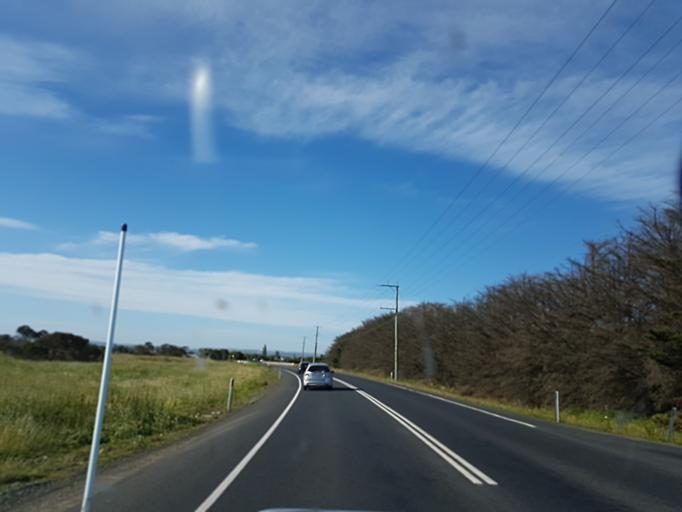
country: AU
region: Victoria
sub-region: Cardinia
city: Pakenham South
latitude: -38.1397
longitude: 145.4886
